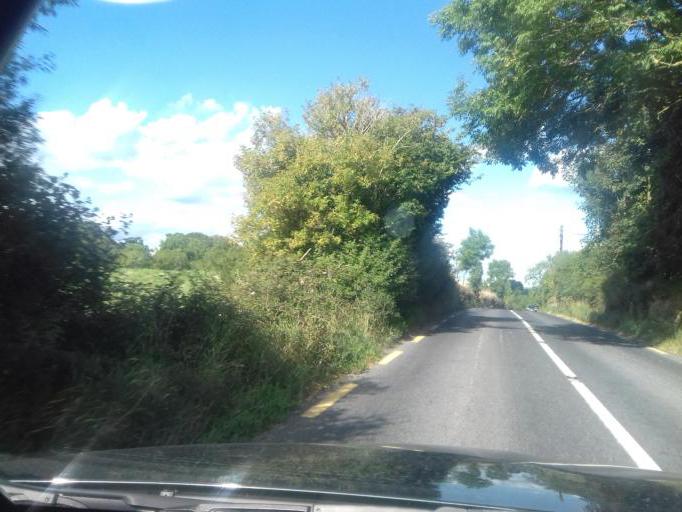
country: IE
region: Leinster
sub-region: Kilkenny
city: Thomastown
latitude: 52.5073
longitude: -7.1624
